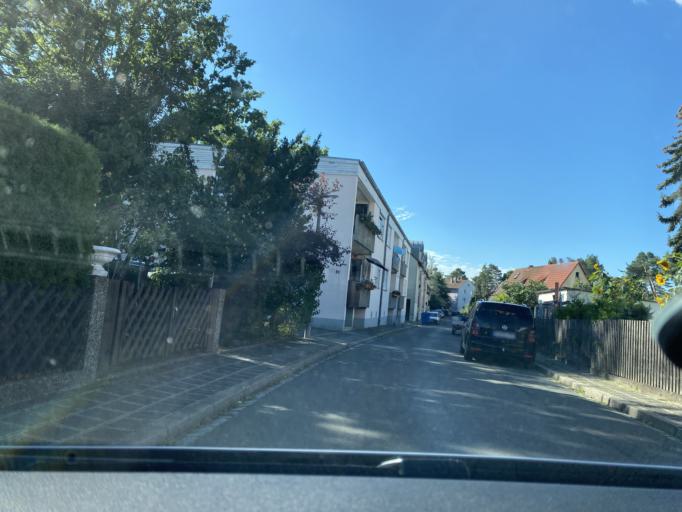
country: DE
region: Bavaria
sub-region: Regierungsbezirk Mittelfranken
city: Furth
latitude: 49.5050
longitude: 10.9825
